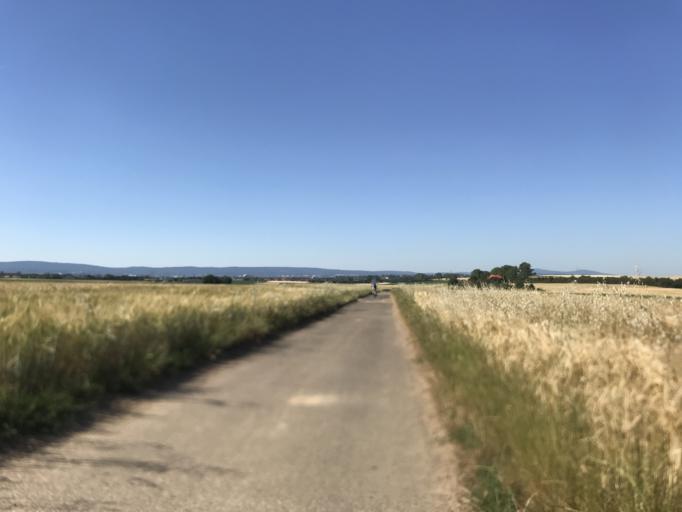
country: DE
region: Rheinland-Pfalz
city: Gau-Bischofsheim
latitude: 49.9304
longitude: 8.2747
